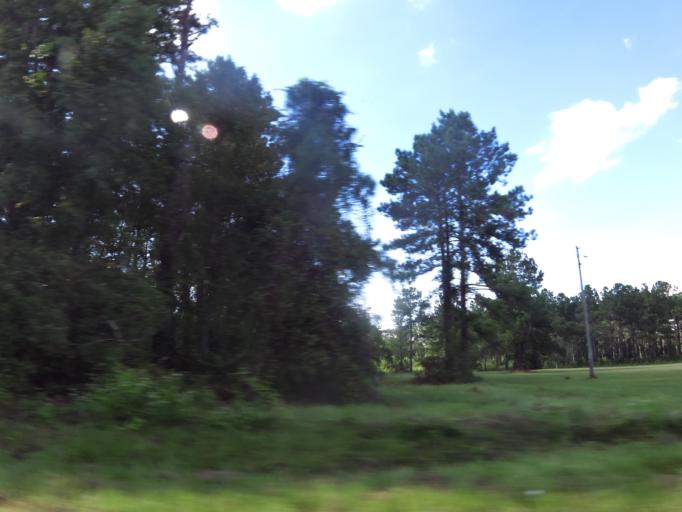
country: US
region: Georgia
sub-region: Brooks County
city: Quitman
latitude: 30.7829
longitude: -83.5882
